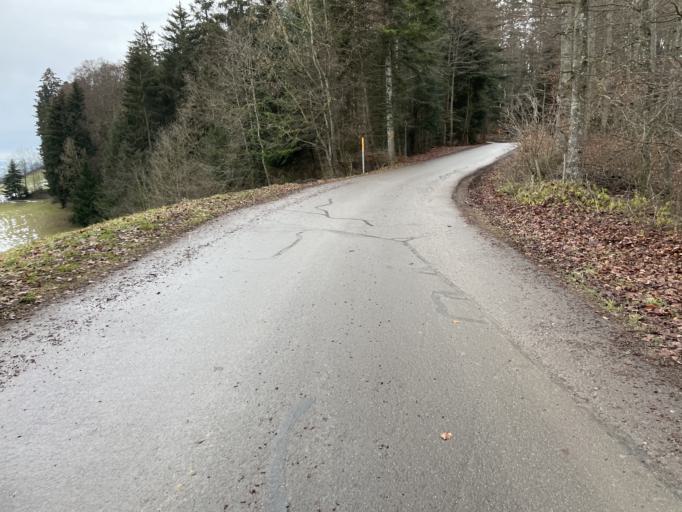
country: CH
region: Bern
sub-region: Bern-Mittelland District
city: Toffen
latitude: 46.8649
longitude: 7.5192
